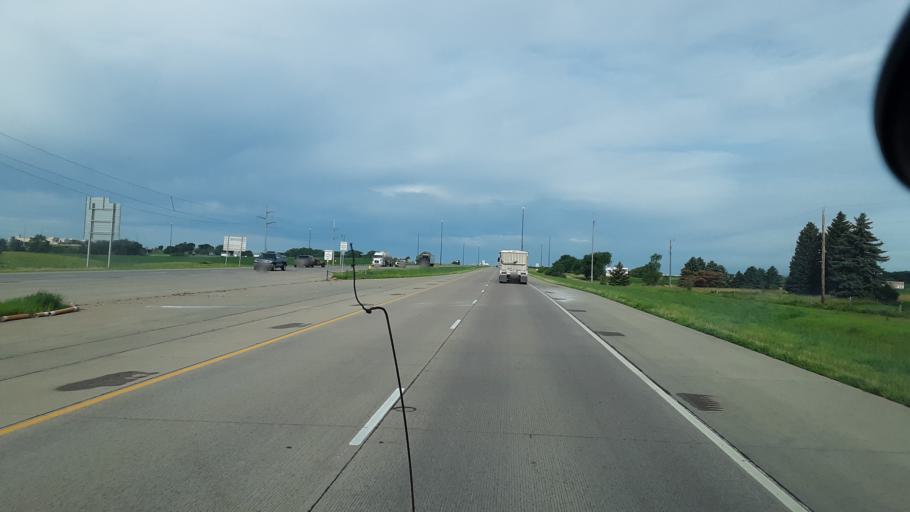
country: US
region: South Dakota
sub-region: Minnehaha County
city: Sioux Falls
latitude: 43.6079
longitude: -96.6781
